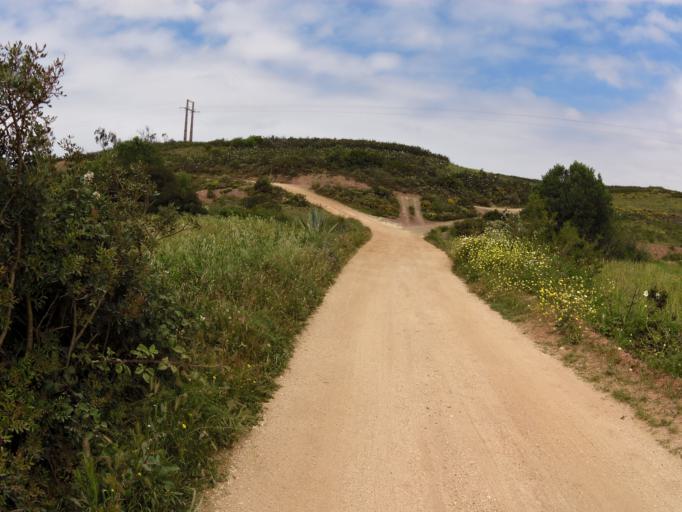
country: PT
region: Faro
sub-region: Vila do Bispo
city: Vila do Bispo
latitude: 37.0861
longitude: -8.8941
